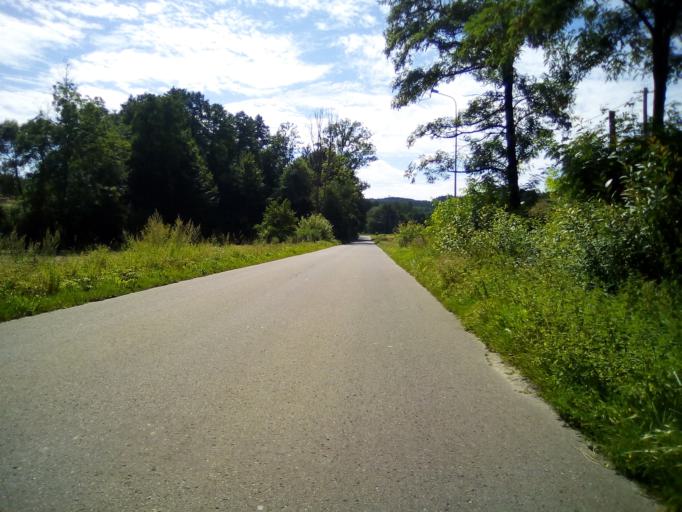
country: PL
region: Subcarpathian Voivodeship
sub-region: Powiat strzyzowski
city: Konieczkowa
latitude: 49.8295
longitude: 21.9300
